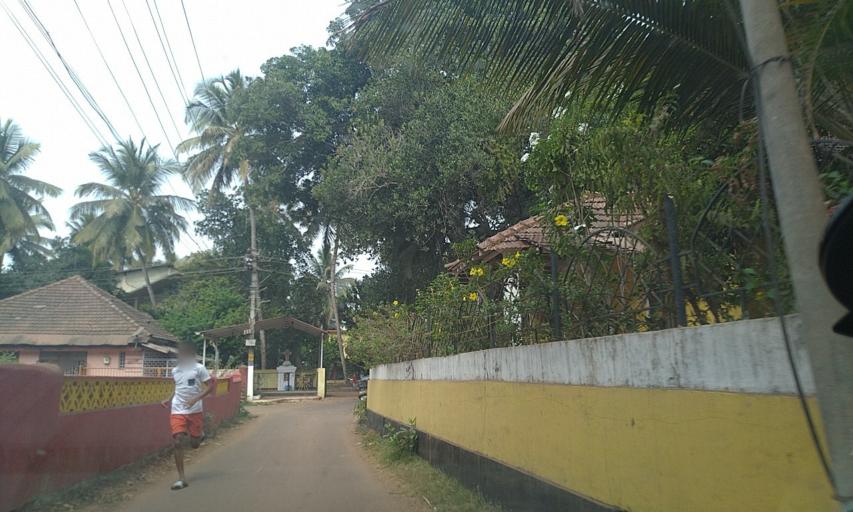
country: IN
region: Goa
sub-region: North Goa
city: Taleigao
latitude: 15.4771
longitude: 73.8422
